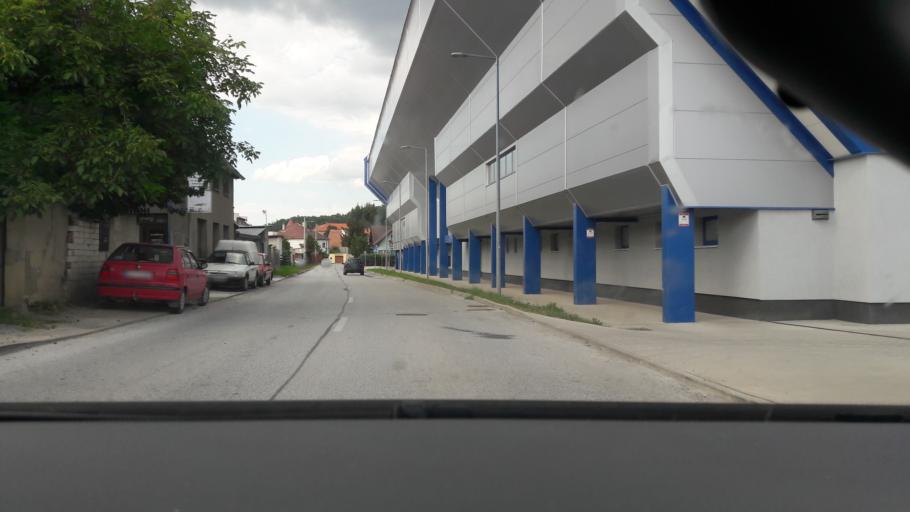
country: SK
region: Presovsky
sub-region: Okres Presov
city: Kezmarok
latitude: 49.1353
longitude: 20.4326
